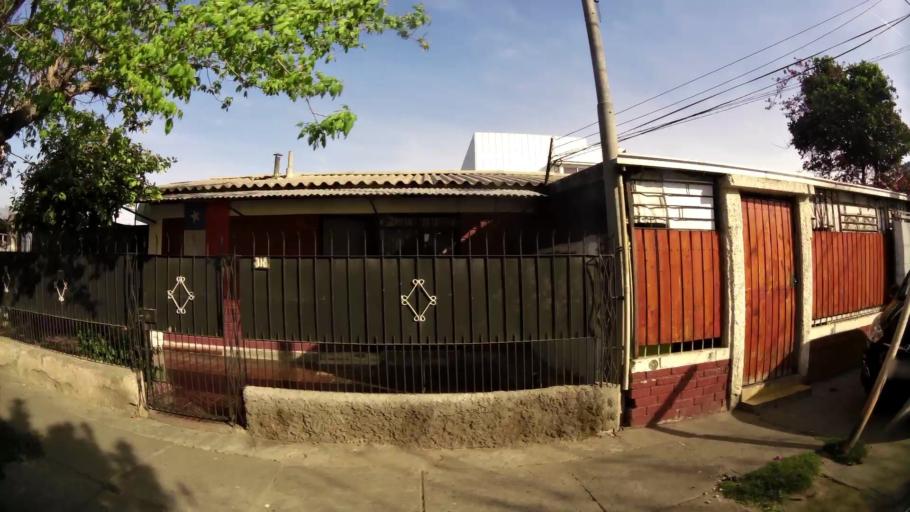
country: CL
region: Santiago Metropolitan
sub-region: Provincia de Santiago
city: Santiago
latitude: -33.5103
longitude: -70.6264
